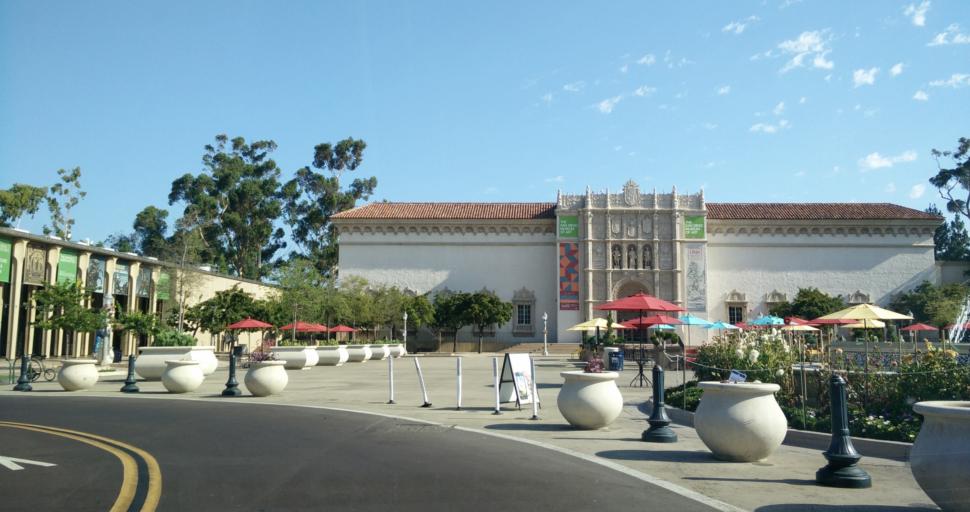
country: US
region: California
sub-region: San Diego County
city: San Diego
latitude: 32.7313
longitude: -117.1505
